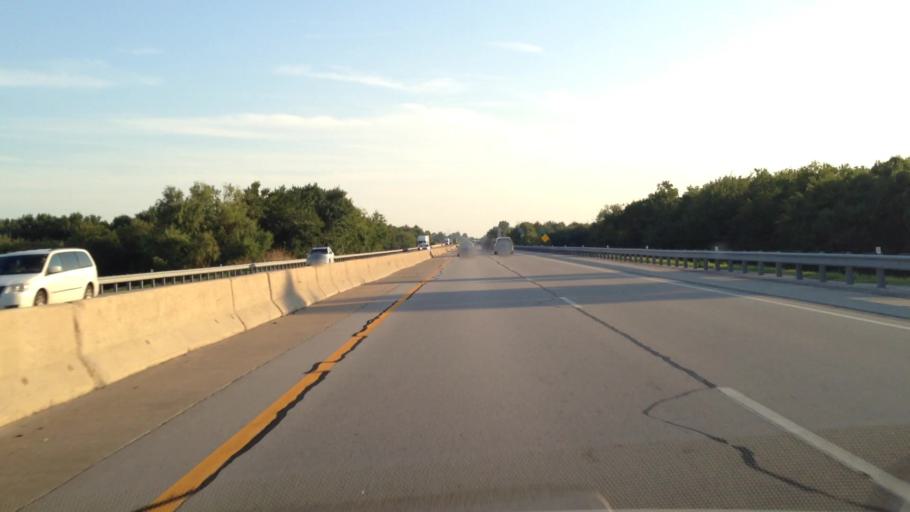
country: US
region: Oklahoma
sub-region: Ottawa County
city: Miami
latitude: 36.8588
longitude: -94.8530
